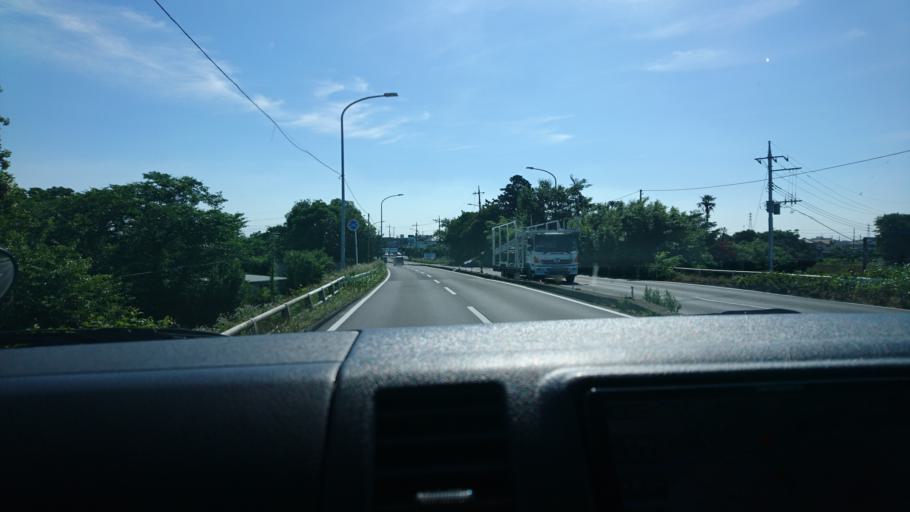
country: JP
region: Saitama
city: Kurihashi
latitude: 36.1251
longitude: 139.6907
